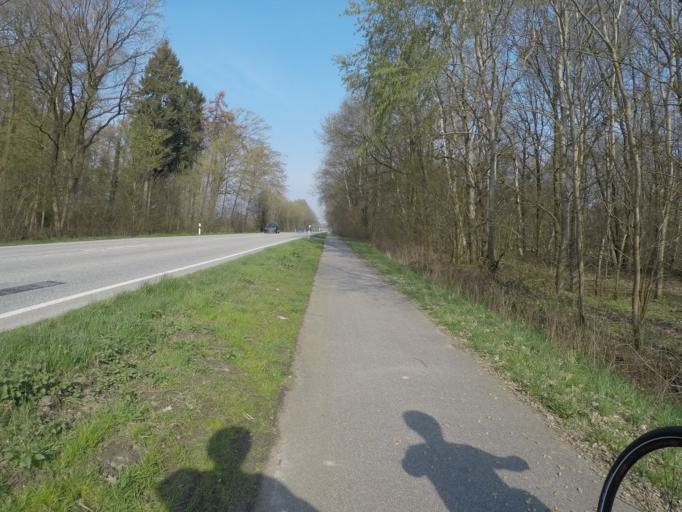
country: DE
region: Schleswig-Holstein
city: Gross Niendorf
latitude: 53.8398
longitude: 10.2291
